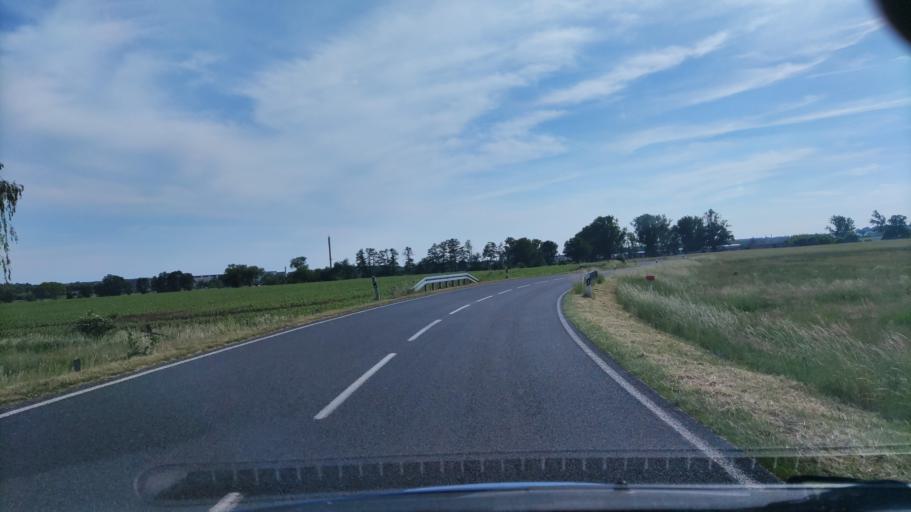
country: DE
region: Saxony-Anhalt
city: Klotze
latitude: 52.6396
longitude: 11.1823
